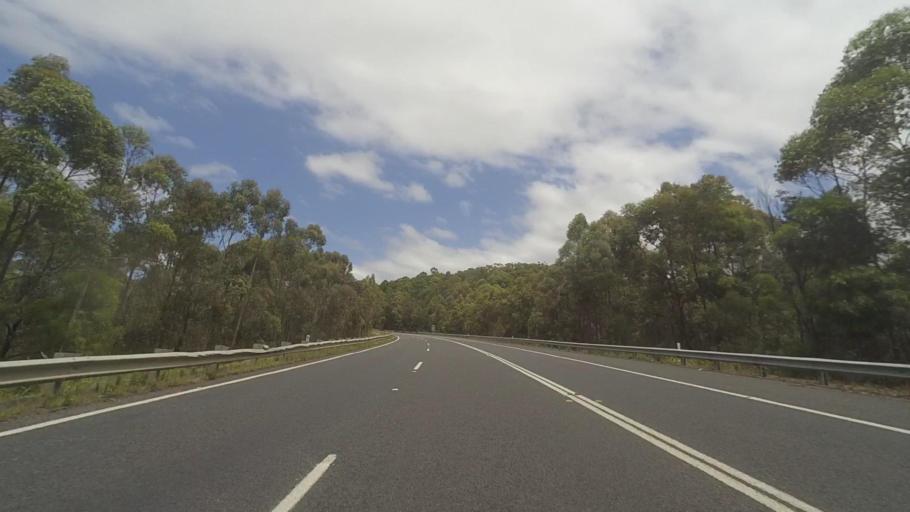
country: AU
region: New South Wales
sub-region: Shoalhaven Shire
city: Milton
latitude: -35.2419
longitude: 150.4267
